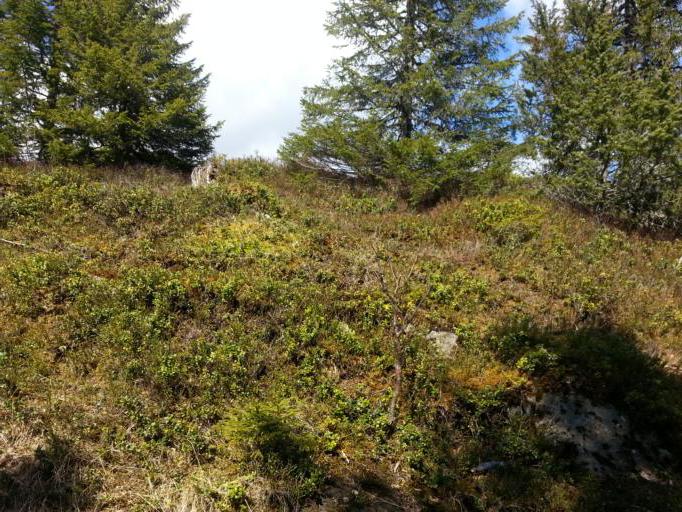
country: NO
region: Nord-Trondelag
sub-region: Levanger
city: Skogn
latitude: 63.5851
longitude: 11.0878
